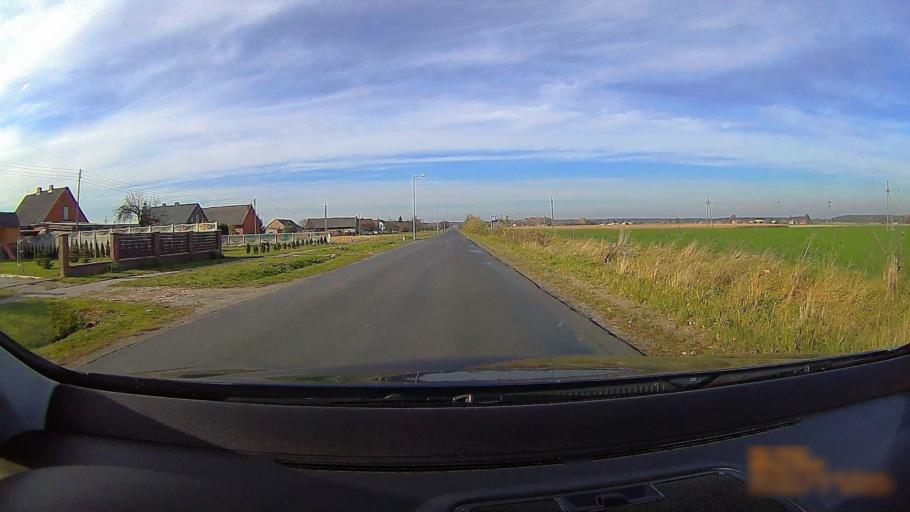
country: PL
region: Greater Poland Voivodeship
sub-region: Powiat ostrzeszowski
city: Doruchow
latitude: 51.4190
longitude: 18.0701
